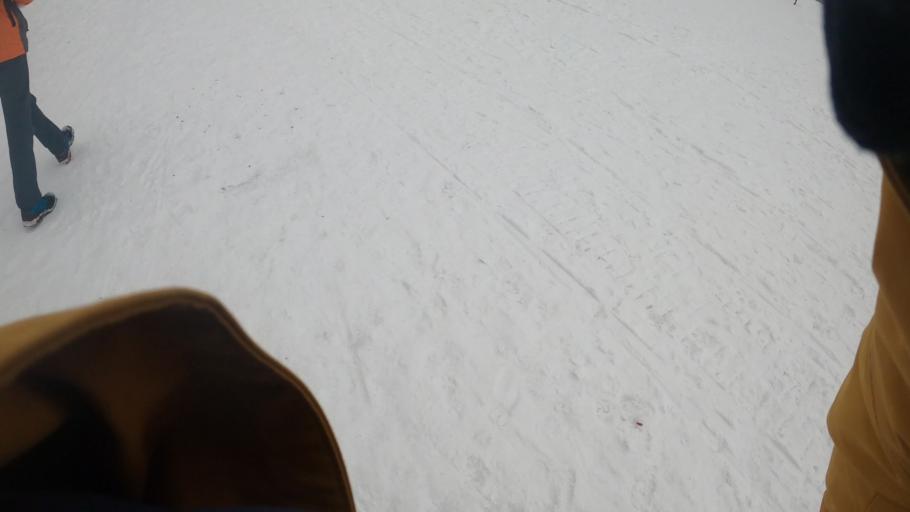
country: RU
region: Jaroslavl
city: Pereslavl'-Zalesskiy
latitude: 56.7359
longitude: 38.8290
